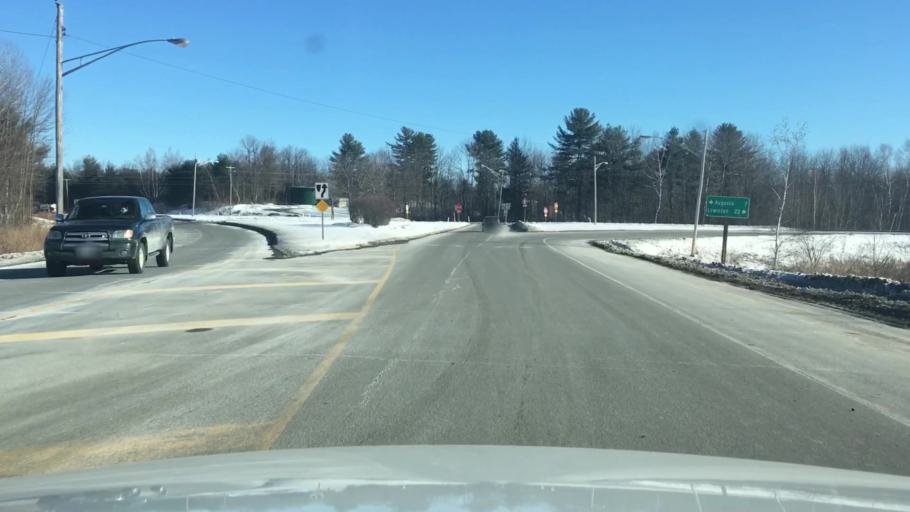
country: US
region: Maine
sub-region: Kennebec County
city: Winthrop
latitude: 44.3071
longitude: -69.9584
